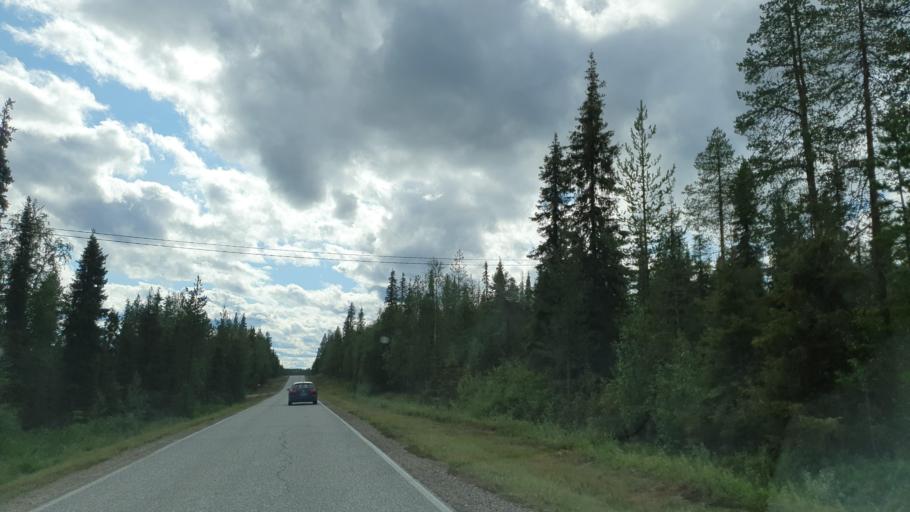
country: FI
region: Lapland
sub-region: Tunturi-Lappi
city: Muonio
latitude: 67.8355
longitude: 24.0774
